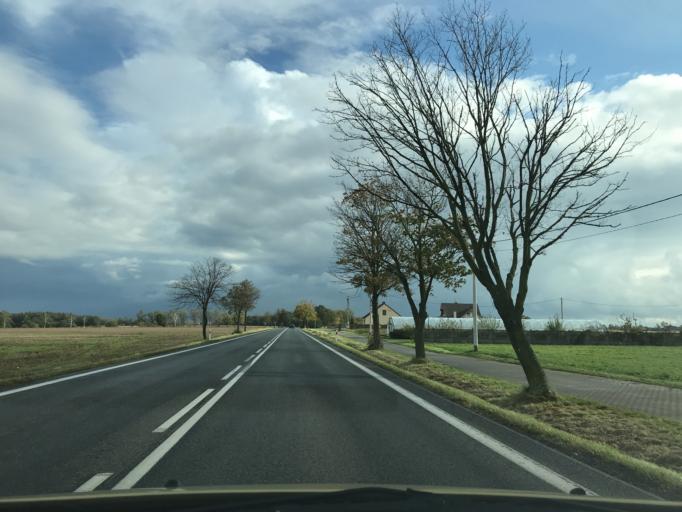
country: PL
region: Greater Poland Voivodeship
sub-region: Powiat ostrowski
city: Nowe Skalmierzyce
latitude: 51.7804
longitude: 18.0146
